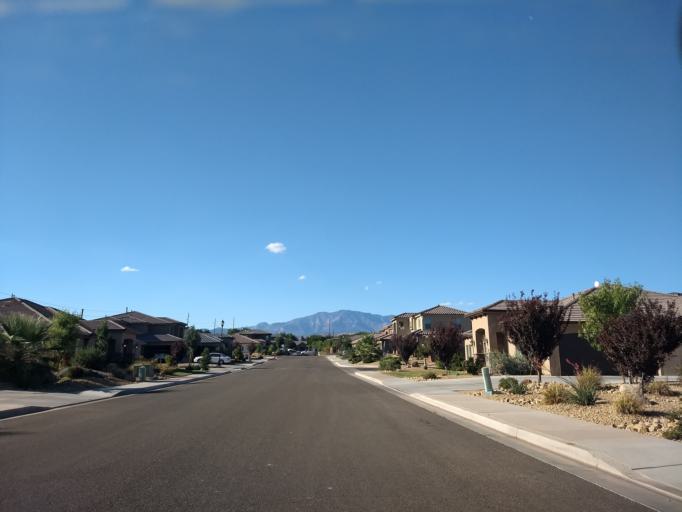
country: US
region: Utah
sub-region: Washington County
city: Washington
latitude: 37.1208
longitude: -113.5076
